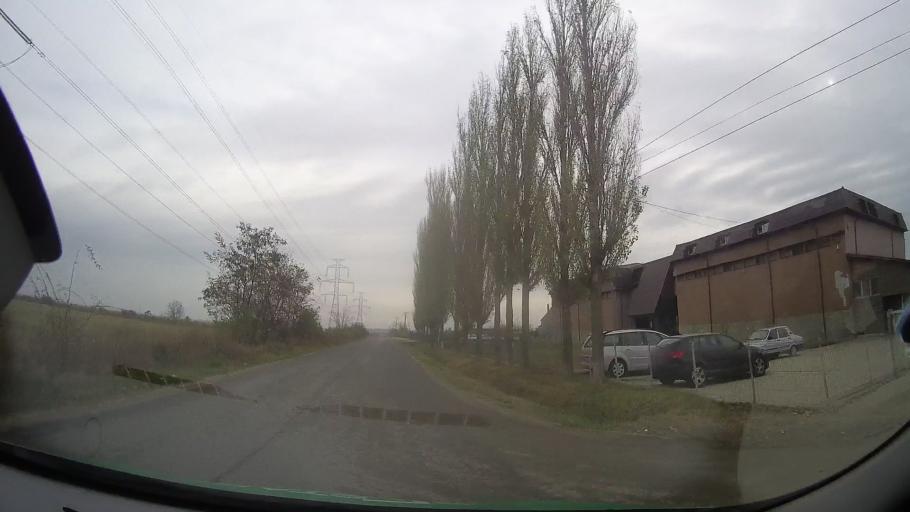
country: RO
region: Prahova
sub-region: Comuna Valea Calugareasca
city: Pantazi
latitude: 44.9293
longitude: 26.1468
